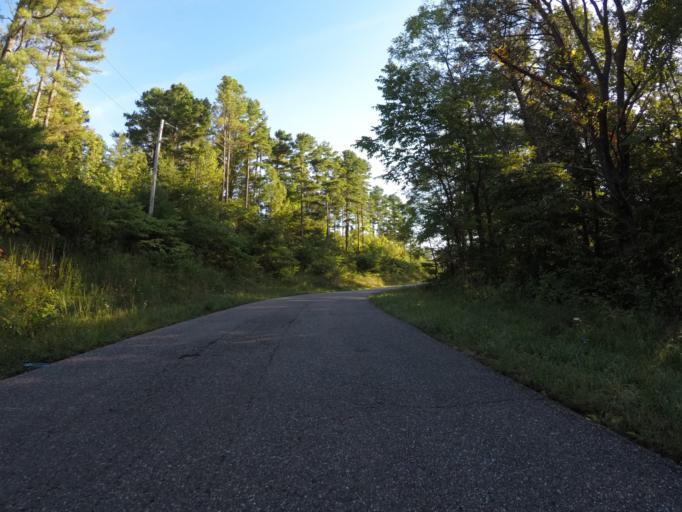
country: US
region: Ohio
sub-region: Lawrence County
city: Coal Grove
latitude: 38.6041
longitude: -82.5608
